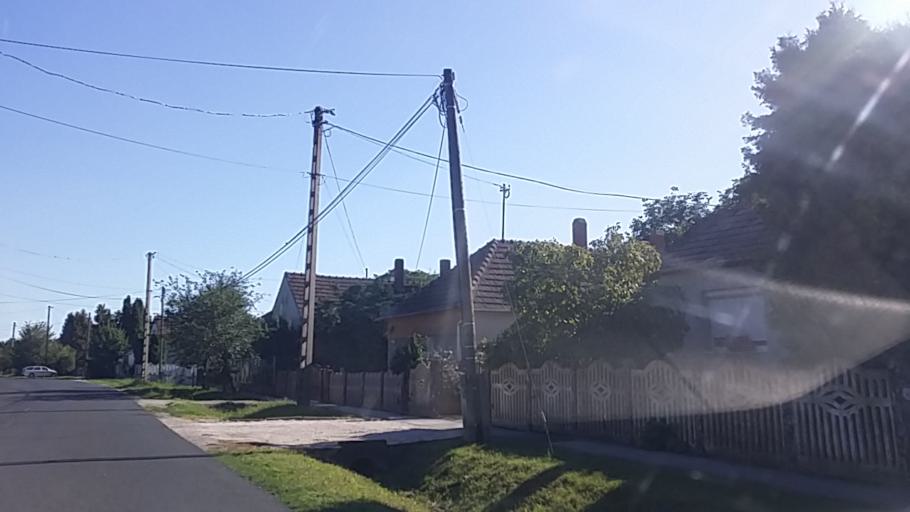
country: HU
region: Zala
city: Sarmellek
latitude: 46.7006
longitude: 17.1668
